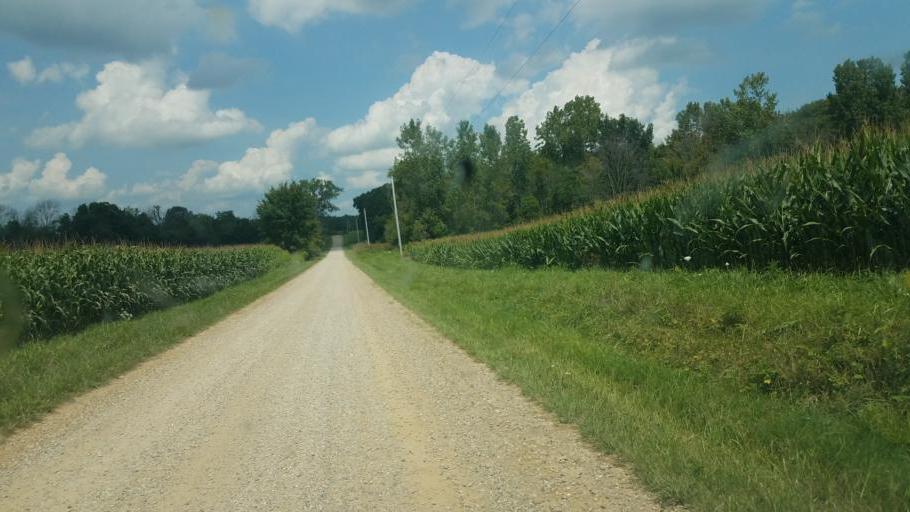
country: US
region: Ohio
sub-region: Knox County
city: Centerburg
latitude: 40.3758
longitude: -82.6332
